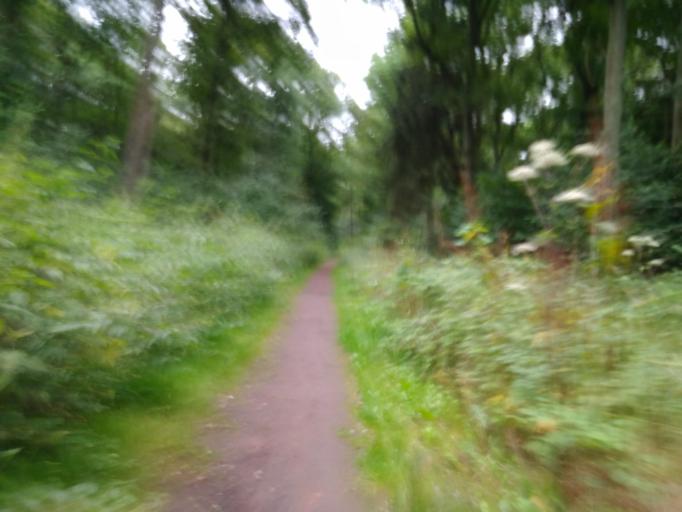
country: DE
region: North Rhine-Westphalia
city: Dorsten
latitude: 51.6218
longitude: 6.9828
